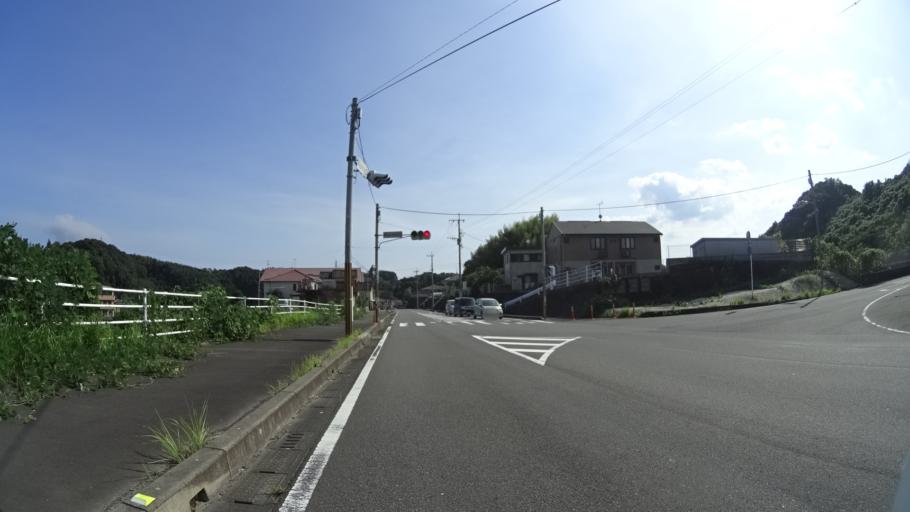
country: JP
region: Kagoshima
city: Kagoshima-shi
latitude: 31.6523
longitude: 130.5523
